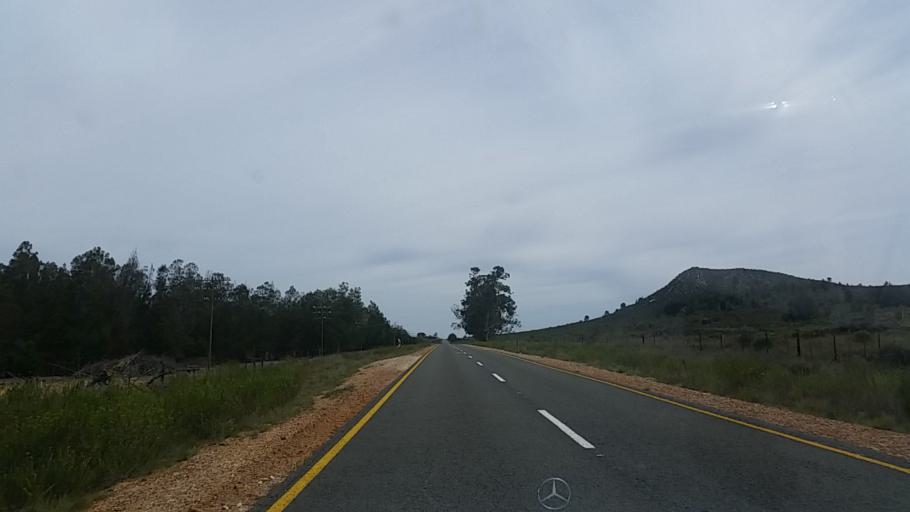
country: ZA
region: Western Cape
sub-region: Eden District Municipality
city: George
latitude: -33.7759
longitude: 22.7055
